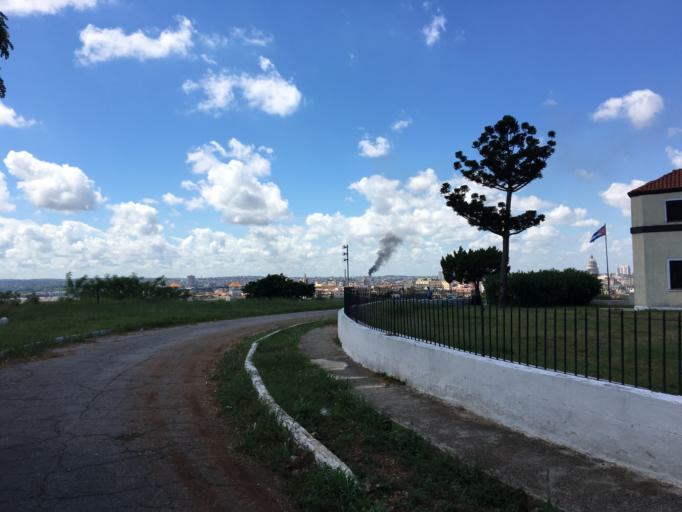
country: CU
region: La Habana
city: La Habana Vieja
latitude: 23.1445
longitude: -82.3451
